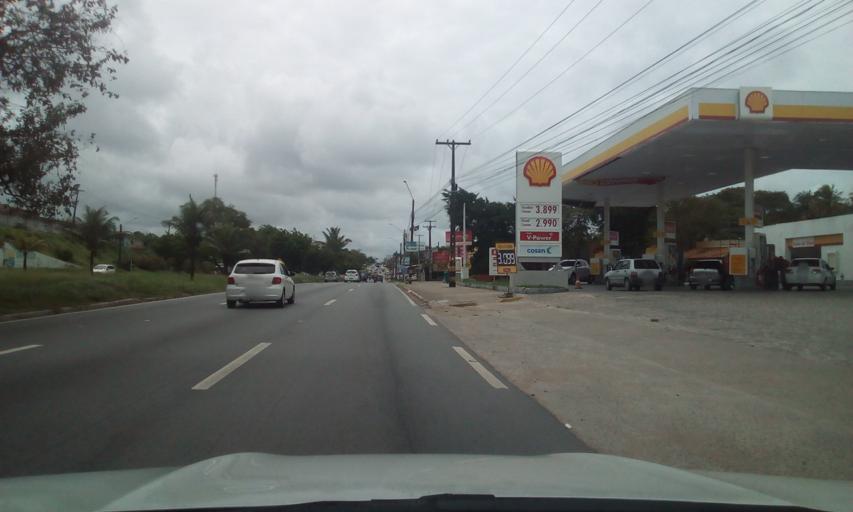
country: BR
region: Pernambuco
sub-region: Abreu E Lima
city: Abreu e Lima
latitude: -7.8841
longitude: -34.9044
